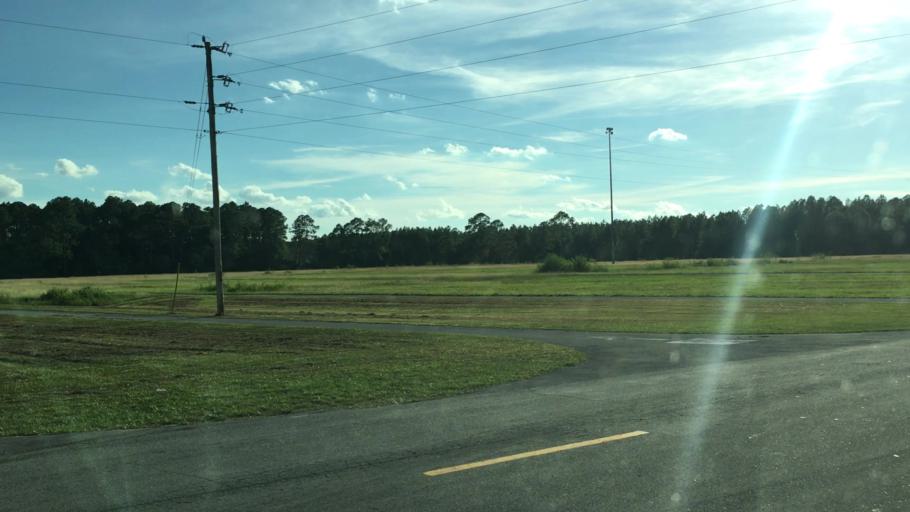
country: US
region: Florida
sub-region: Alachua County
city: Waldo
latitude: 29.7563
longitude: -82.2749
